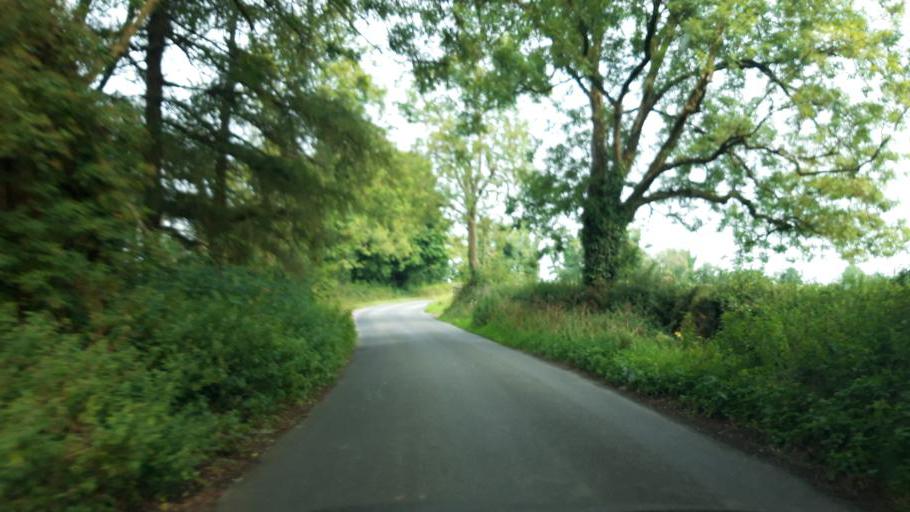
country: IE
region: Munster
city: Fethard
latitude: 52.5774
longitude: -7.5856
